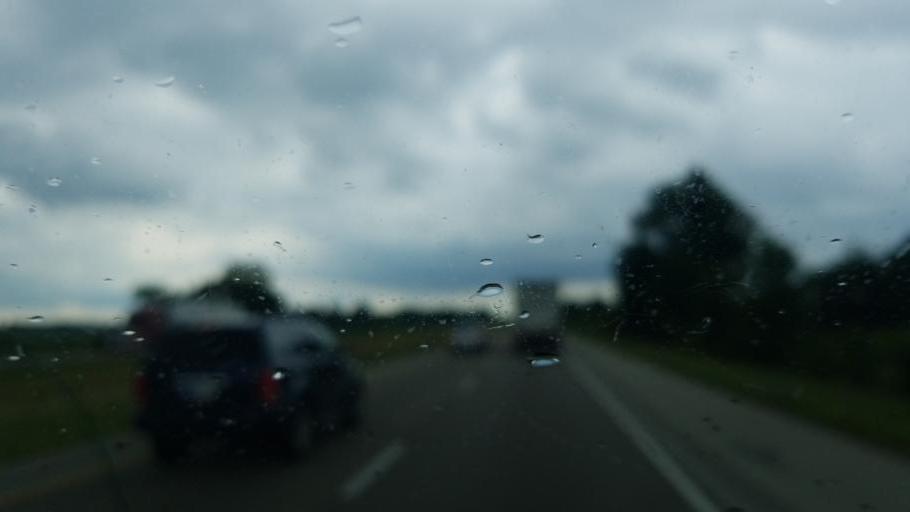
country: US
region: Illinois
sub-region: Cumberland County
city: Toledo
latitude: 39.2274
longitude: -88.2240
